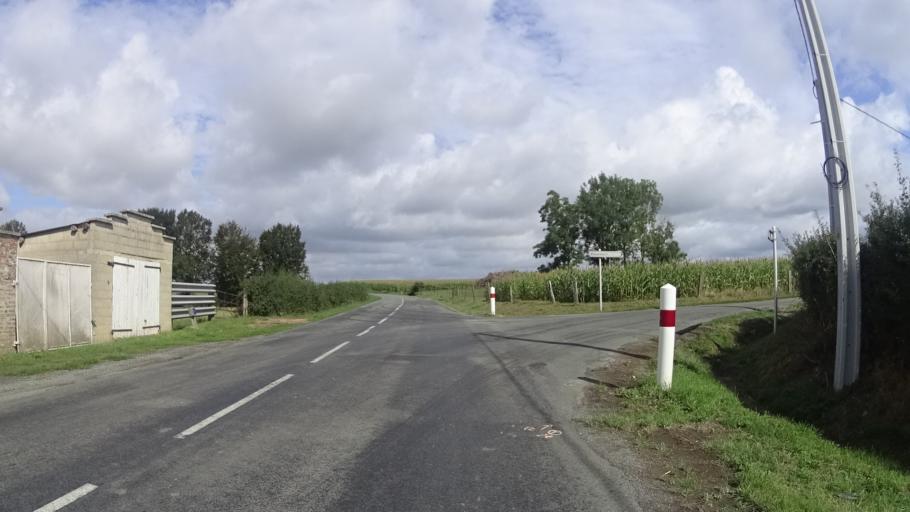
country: FR
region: Nord-Pas-de-Calais
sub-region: Departement du Nord
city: Landrecies
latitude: 50.0816
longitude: 3.6490
